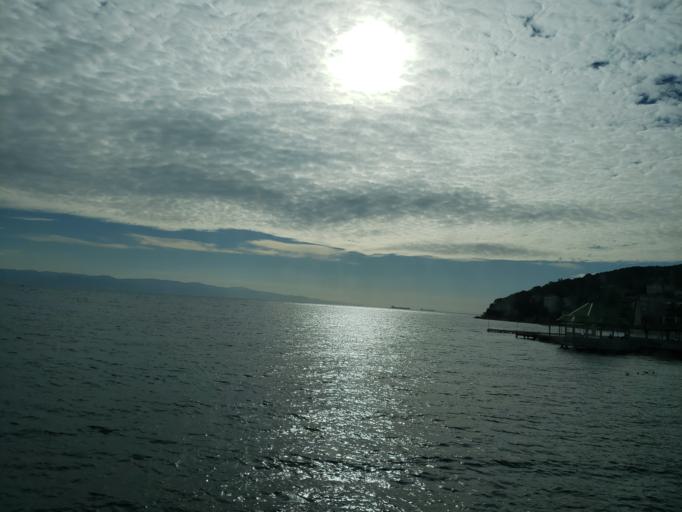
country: TR
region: Istanbul
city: Adalan
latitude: 40.8798
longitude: 29.0735
